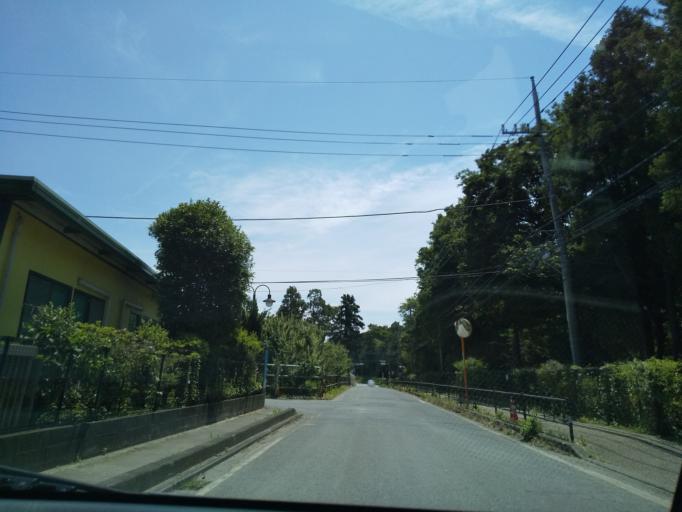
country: JP
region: Kanagawa
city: Zama
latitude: 35.5268
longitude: 139.3933
